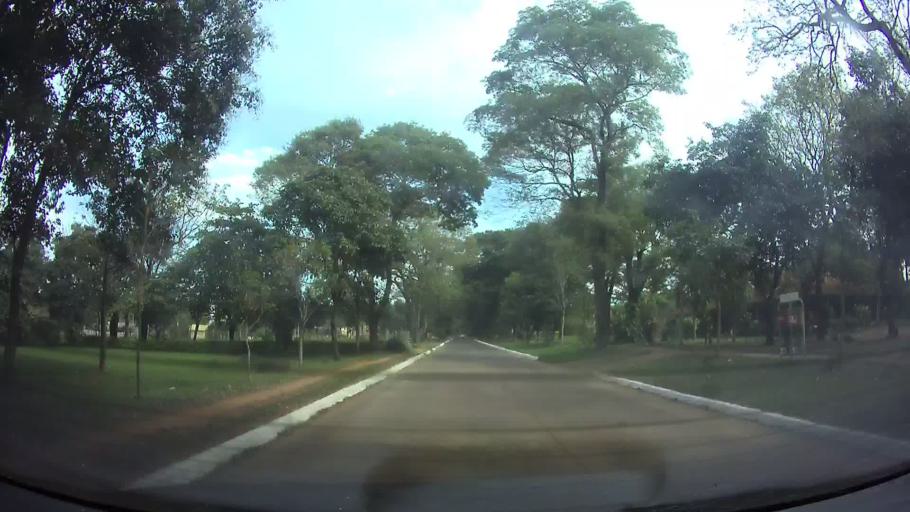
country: PY
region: Central
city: Fernando de la Mora
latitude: -25.3374
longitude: -57.5175
